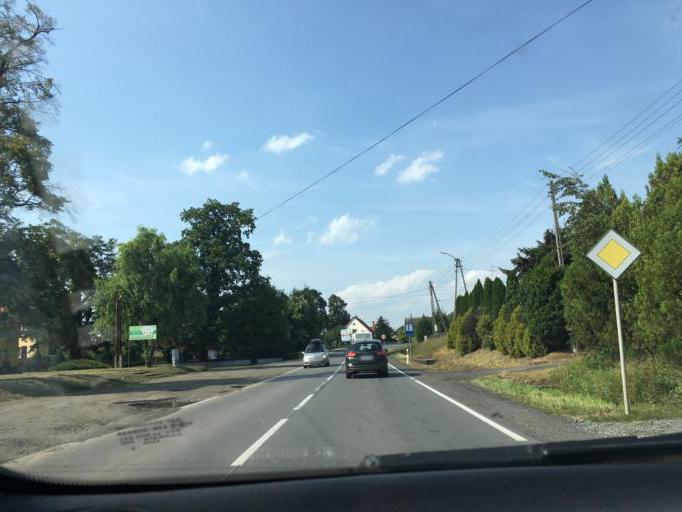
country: PL
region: Opole Voivodeship
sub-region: Powiat prudnicki
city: Prudnik
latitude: 50.3426
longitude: 17.5594
